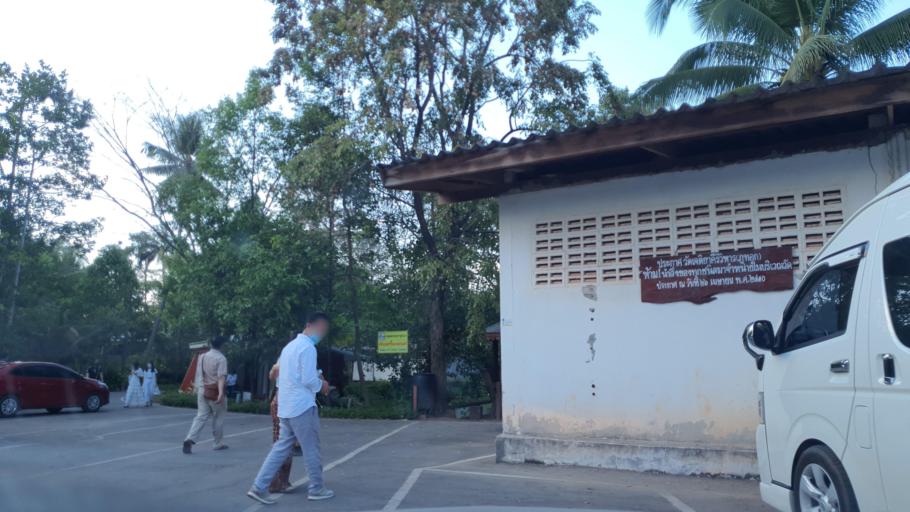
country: TH
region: Changwat Bueng Kan
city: Si Wilai
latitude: 18.1310
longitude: 103.8802
